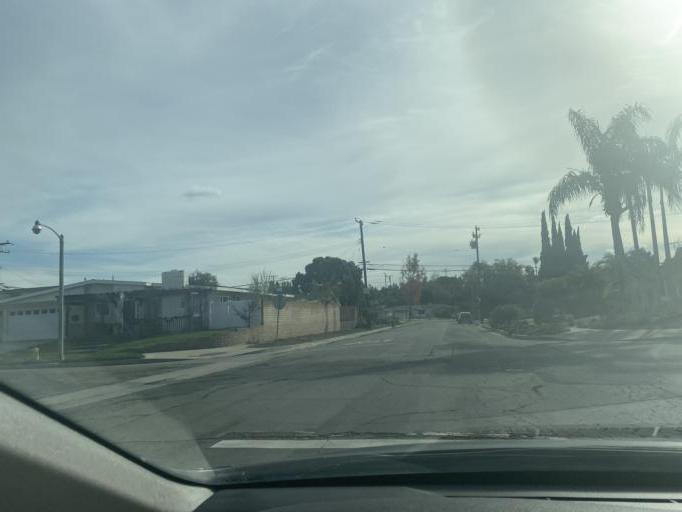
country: US
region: California
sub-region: Orange County
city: Brea
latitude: 33.9068
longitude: -117.8938
